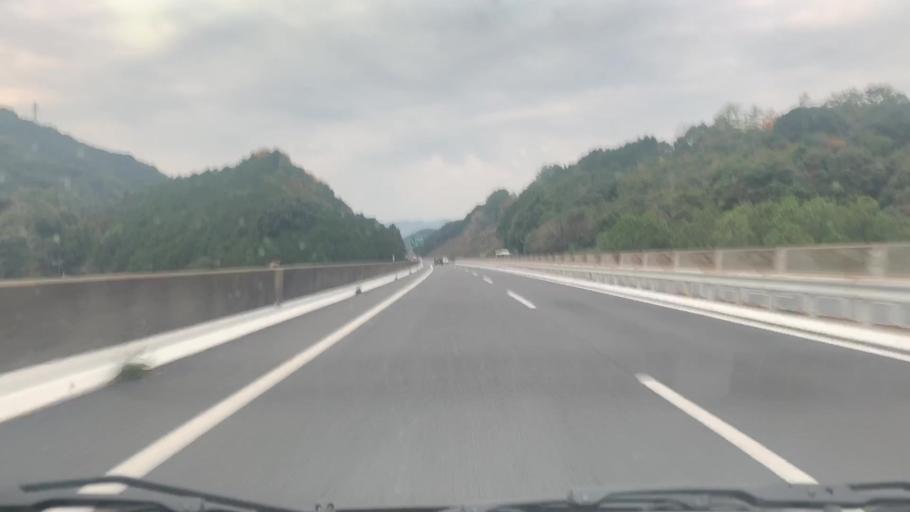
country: JP
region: Nagasaki
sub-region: Isahaya-shi
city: Isahaya
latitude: 32.8193
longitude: 129.9808
